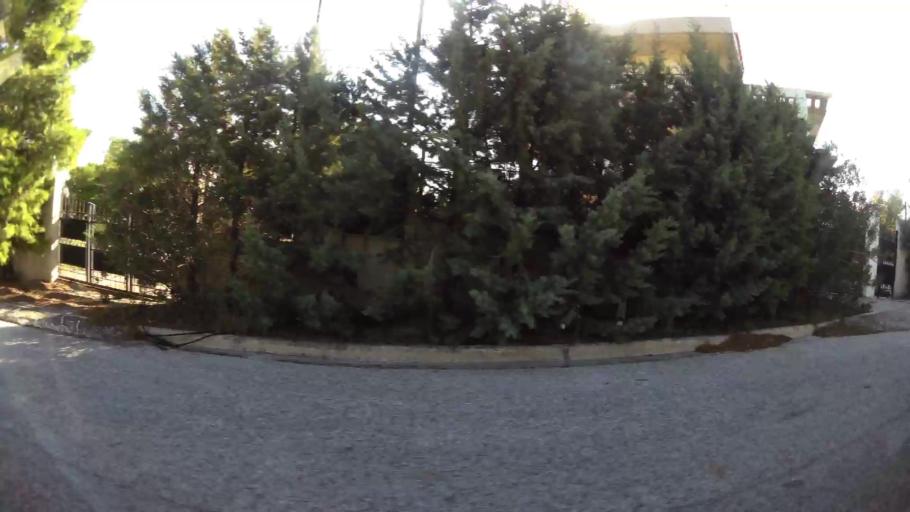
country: GR
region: Attica
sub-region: Nomarchia Anatolikis Attikis
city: Dhrafi
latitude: 38.0271
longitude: 23.8944
